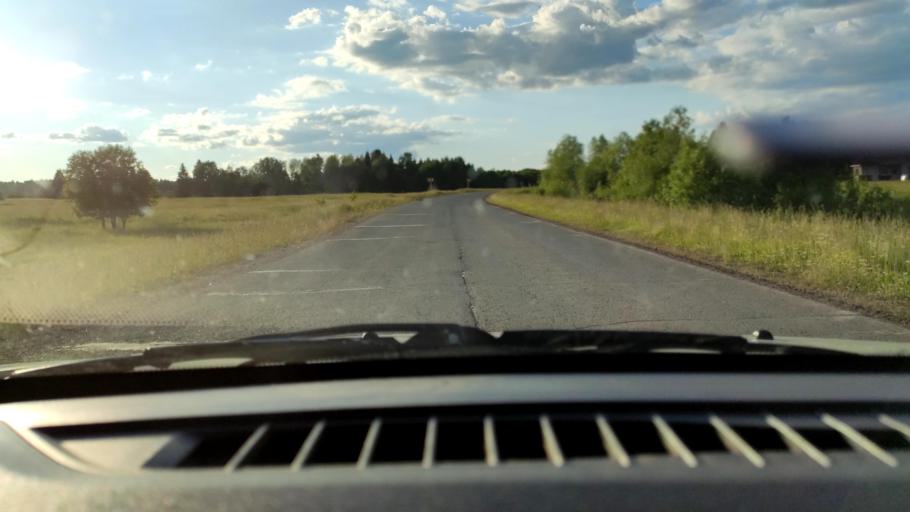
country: RU
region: Perm
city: Uinskoye
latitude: 57.0789
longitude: 56.5551
